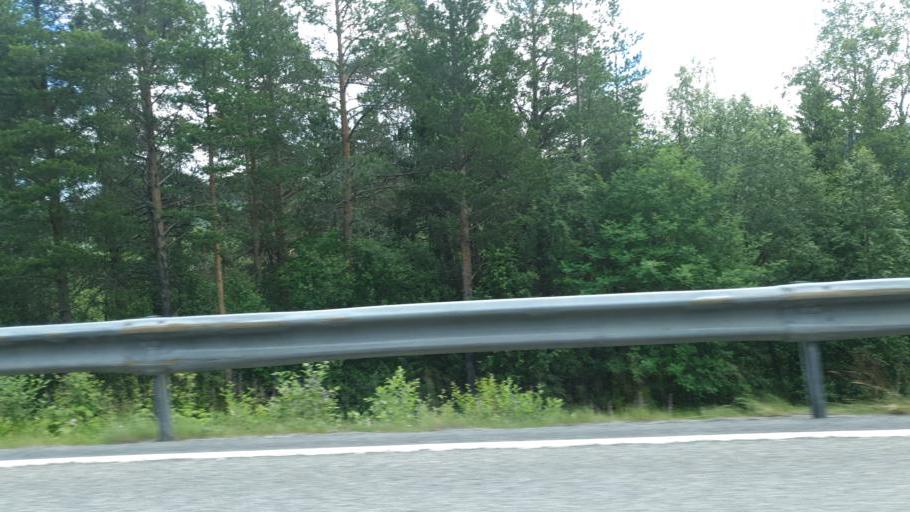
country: NO
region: Sor-Trondelag
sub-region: Rennebu
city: Berkak
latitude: 62.6662
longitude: 9.8971
